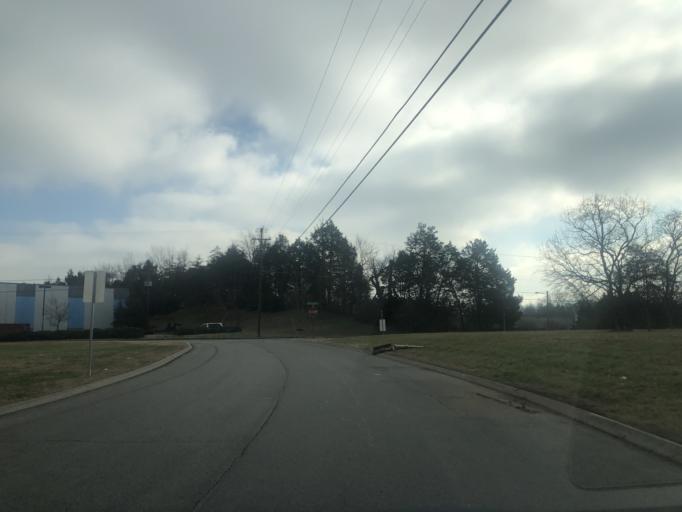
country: US
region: Tennessee
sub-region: Rutherford County
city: La Vergne
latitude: 36.0780
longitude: -86.6473
